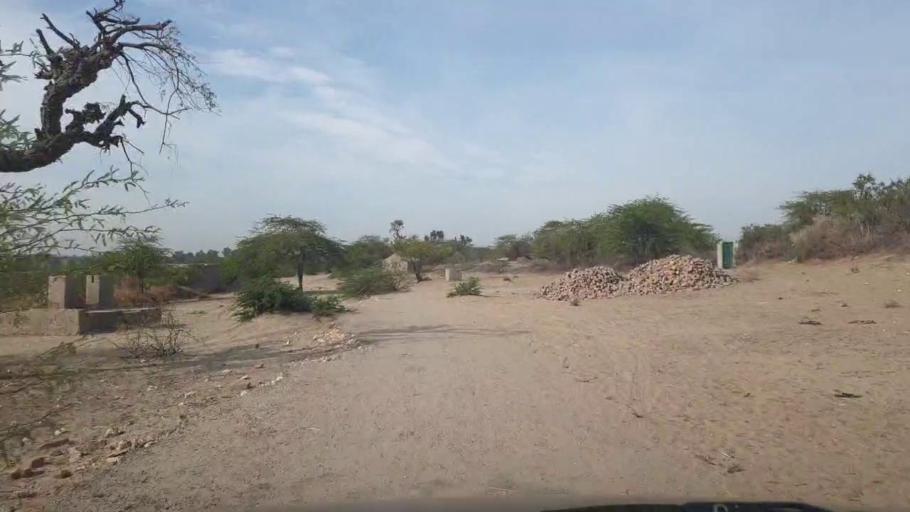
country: PK
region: Sindh
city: Umarkot
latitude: 25.3081
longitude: 69.7060
